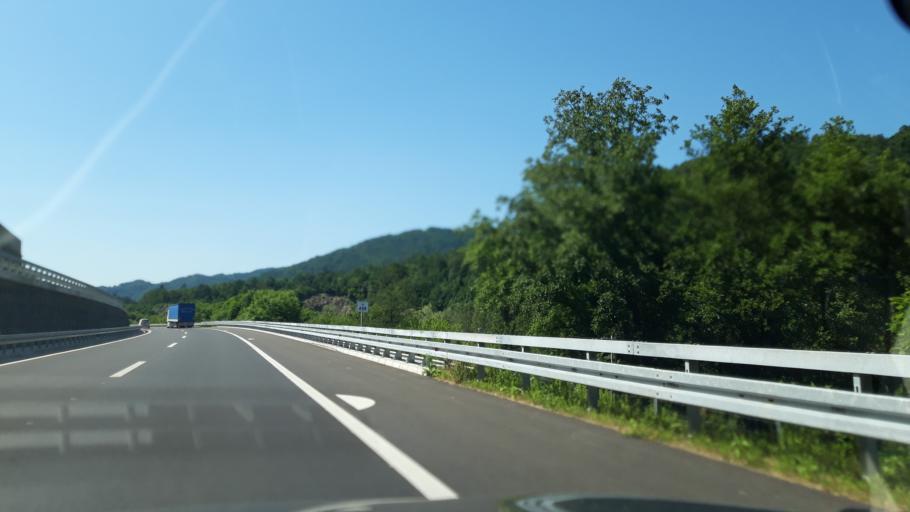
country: RS
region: Central Serbia
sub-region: Jablanicki Okrug
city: Vlasotince
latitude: 42.8524
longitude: 22.1269
